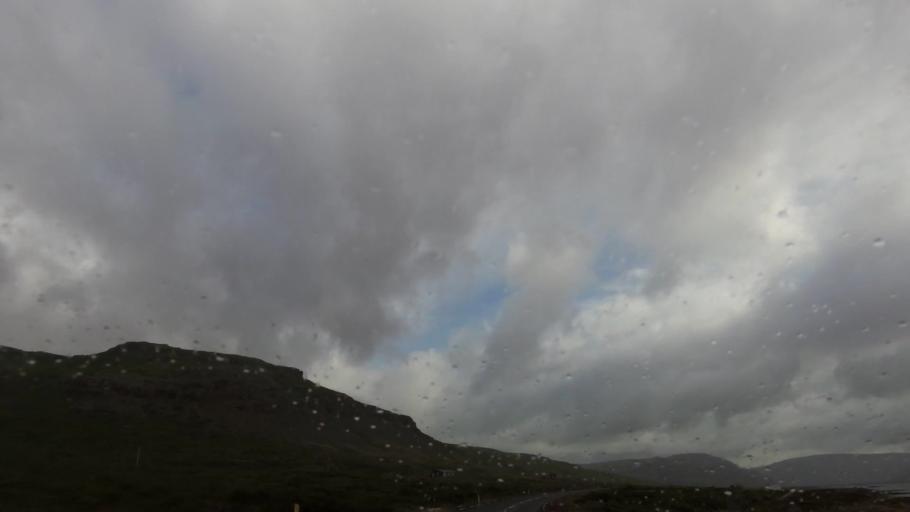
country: IS
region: Westfjords
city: Isafjoerdur
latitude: 65.5474
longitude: -23.2025
